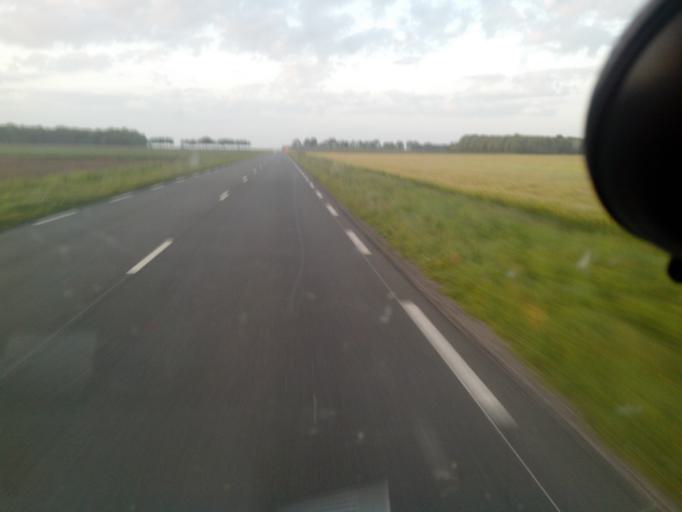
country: FR
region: Picardie
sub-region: Departement de la Somme
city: Crecy-en-Ponthieu
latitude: 50.2007
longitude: 1.8927
